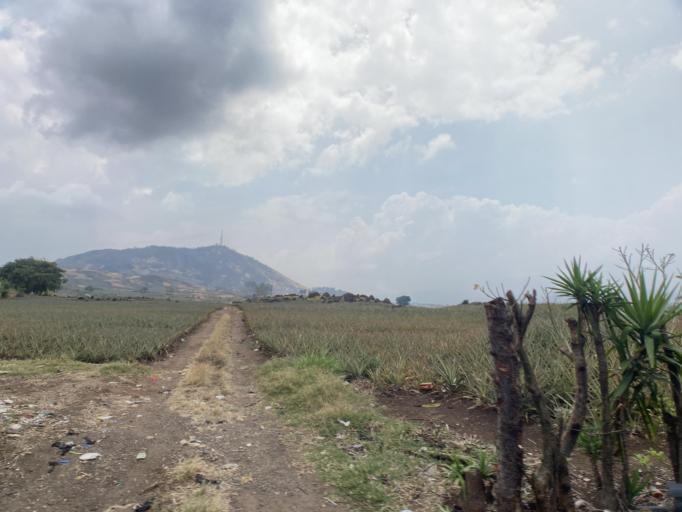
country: GT
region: Guatemala
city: Fraijanes
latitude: 14.3663
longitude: -90.4946
